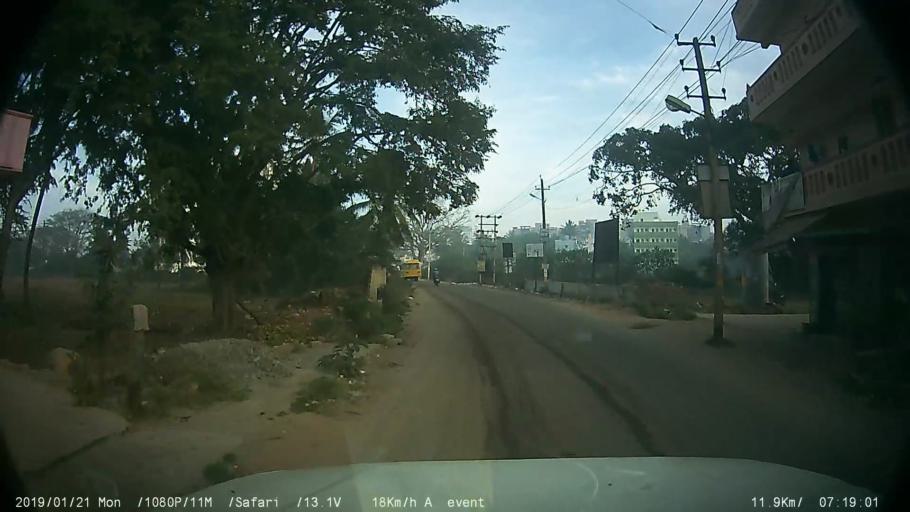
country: IN
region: Karnataka
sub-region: Bangalore Urban
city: Anekal
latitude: 12.8286
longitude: 77.6553
